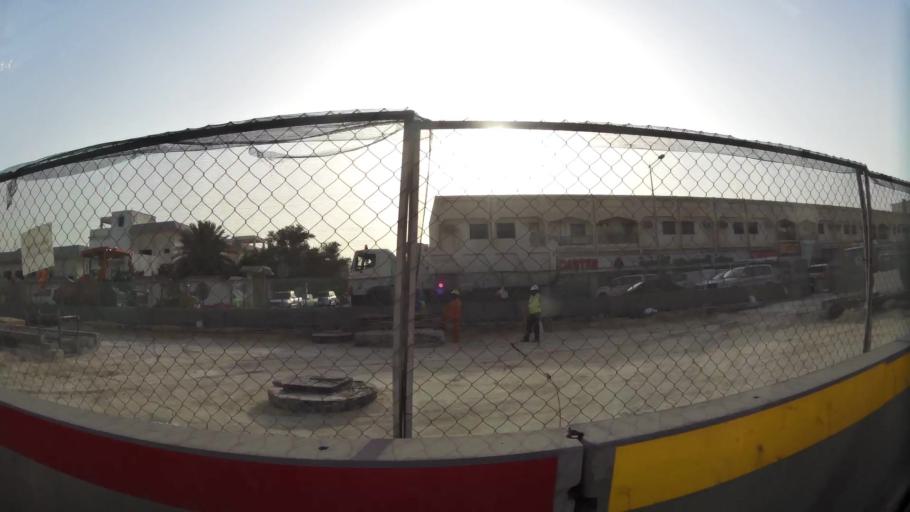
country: QA
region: Baladiyat ar Rayyan
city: Ar Rayyan
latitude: 25.2504
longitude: 51.4517
